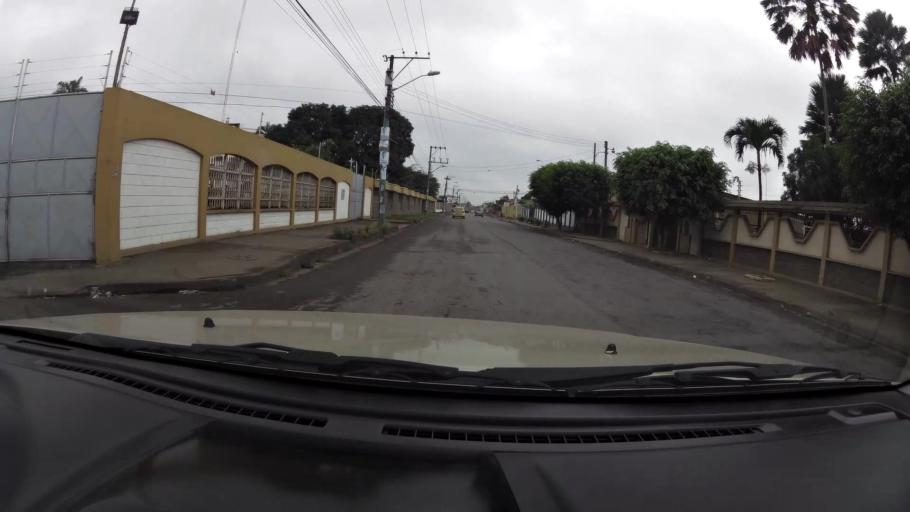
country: EC
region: El Oro
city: Pasaje
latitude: -3.3271
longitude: -79.8187
